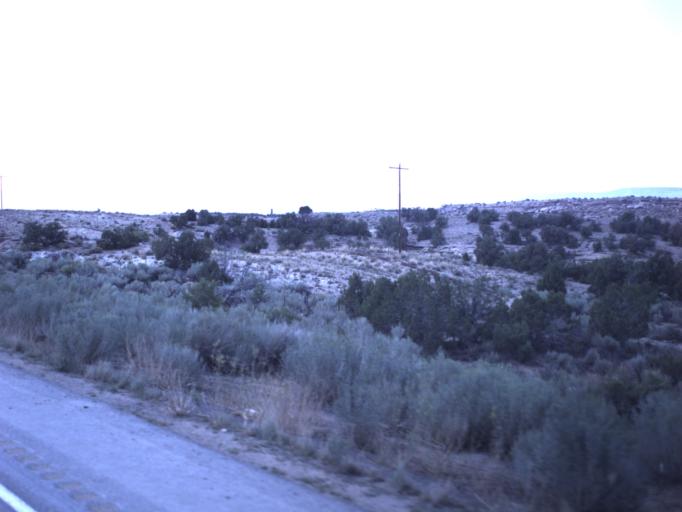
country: US
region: Utah
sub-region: Duchesne County
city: Duchesne
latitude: 40.1642
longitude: -110.4442
